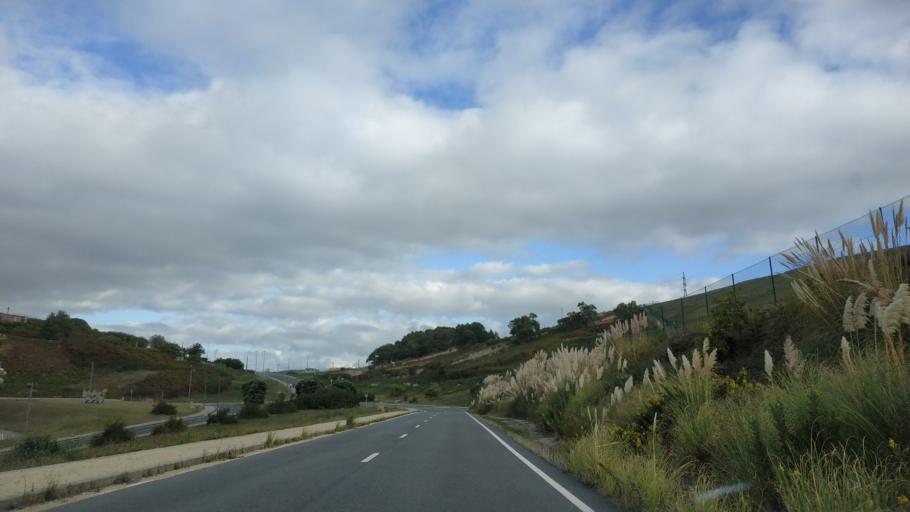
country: ES
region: Galicia
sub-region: Provincia da Coruna
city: A Coruna
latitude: 43.3709
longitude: -8.4454
